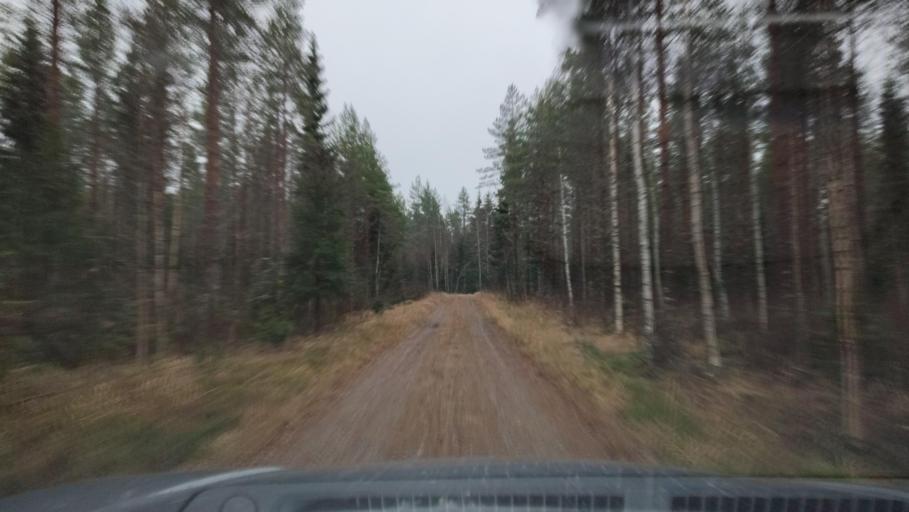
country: FI
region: Southern Ostrobothnia
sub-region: Suupohja
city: Karijoki
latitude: 62.1466
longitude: 21.5930
